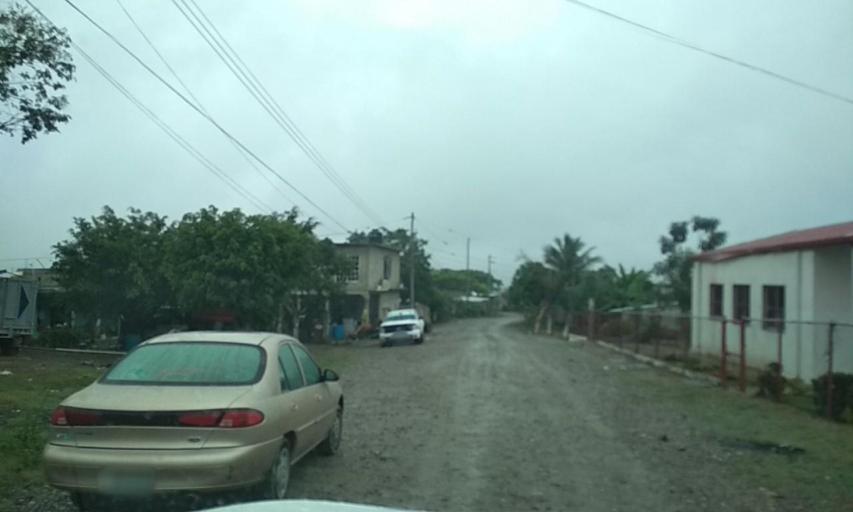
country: MX
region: Veracruz
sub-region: Papantla
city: El Chote
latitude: 20.3582
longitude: -97.3407
